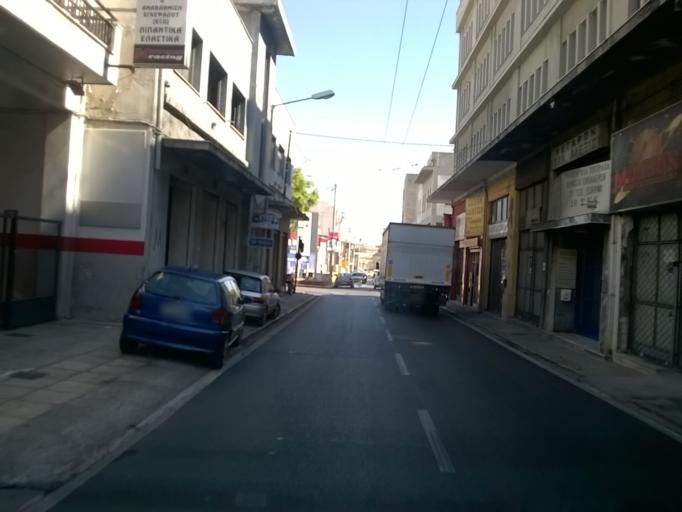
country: GR
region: Attica
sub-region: Nomos Attikis
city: Piraeus
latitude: 37.9491
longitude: 23.6479
